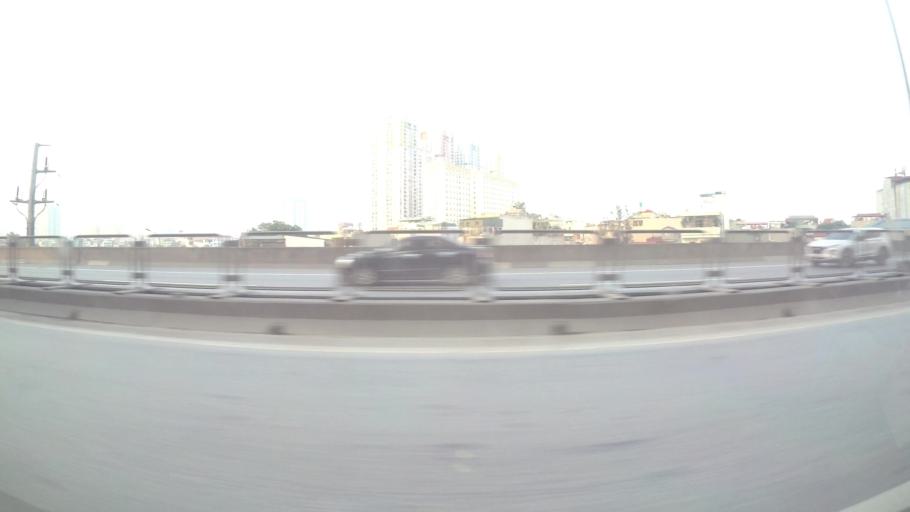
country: VN
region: Ha Noi
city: Thanh Xuan
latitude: 20.9835
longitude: 105.8091
